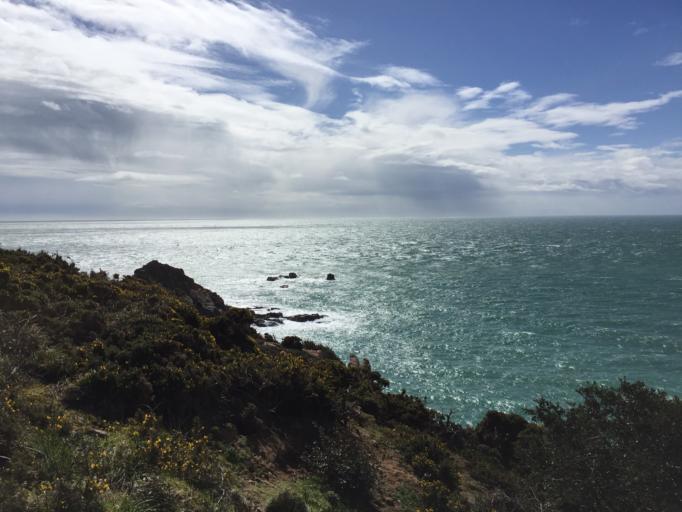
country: JE
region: St Helier
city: Saint Helier
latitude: 49.1701
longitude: -2.1738
